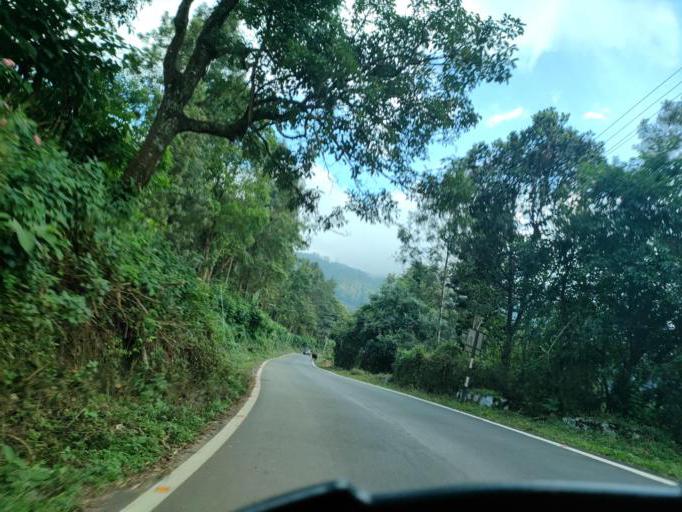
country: IN
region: Tamil Nadu
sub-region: Dindigul
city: Kodaikanal
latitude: 10.2707
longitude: 77.5336
